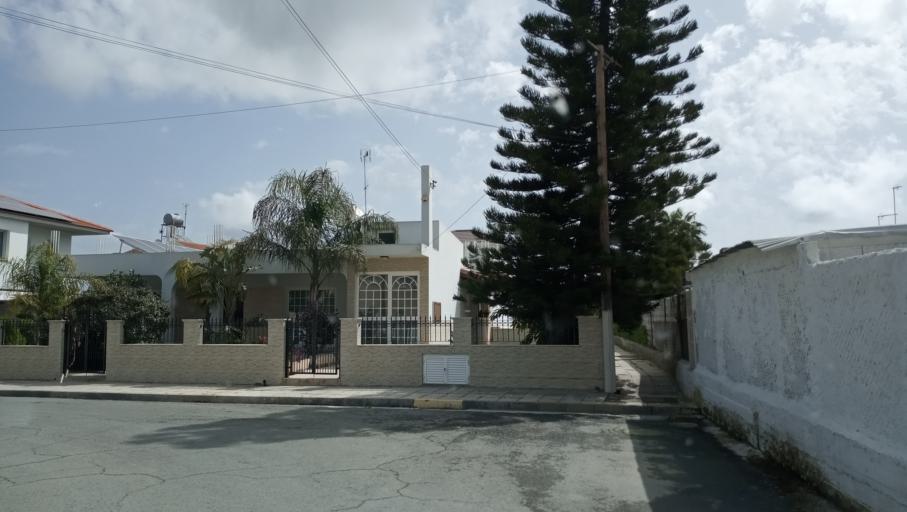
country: CY
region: Lefkosia
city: Dali
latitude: 35.0217
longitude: 33.4260
